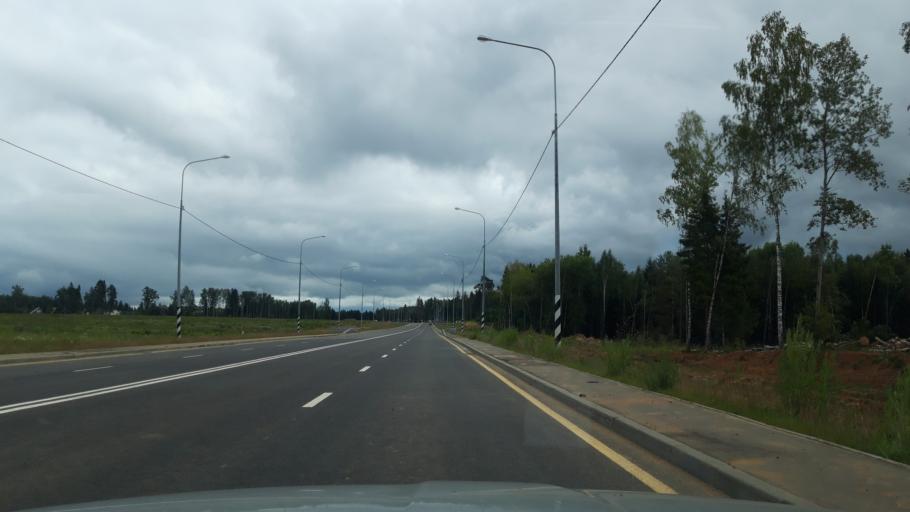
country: RU
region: Moskovskaya
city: Lozhki
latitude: 56.0803
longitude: 37.1040
